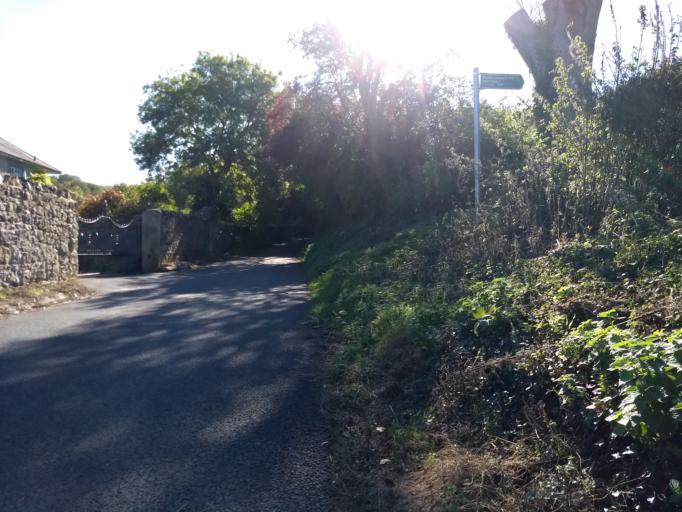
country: GB
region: England
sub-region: Isle of Wight
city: Ventnor
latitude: 50.6046
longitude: -1.2288
